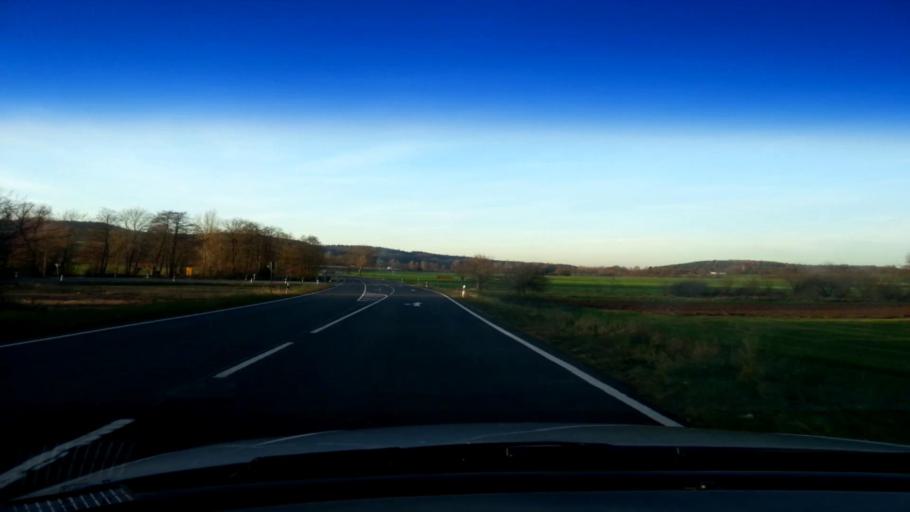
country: DE
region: Bavaria
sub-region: Upper Franconia
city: Rattelsdorf
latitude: 50.0204
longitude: 10.8872
